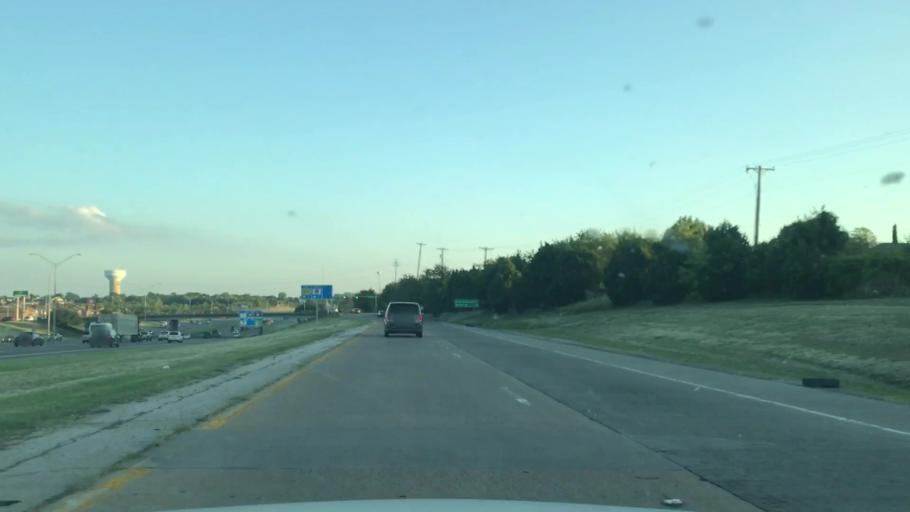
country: US
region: Texas
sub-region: Dallas County
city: Mesquite
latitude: 32.7509
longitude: -96.6154
